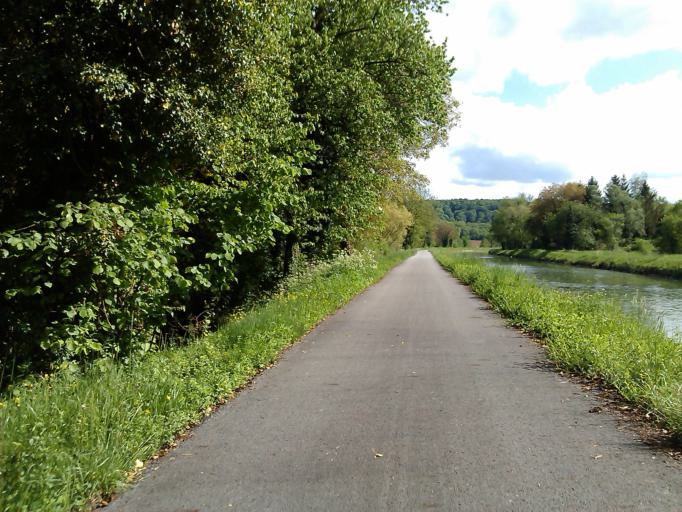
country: FR
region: Franche-Comte
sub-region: Departement du Doubs
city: Colombier-Fontaine
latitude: 47.4370
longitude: 6.6296
